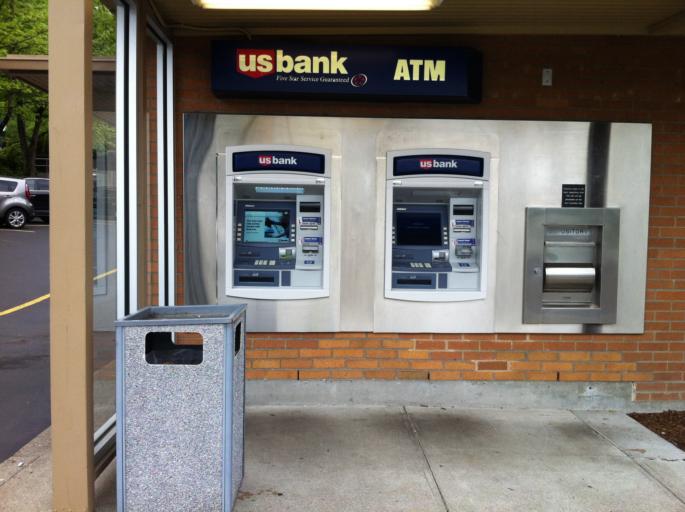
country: US
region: Oregon
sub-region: Multnomah County
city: Portland
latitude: 45.4717
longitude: -122.6852
